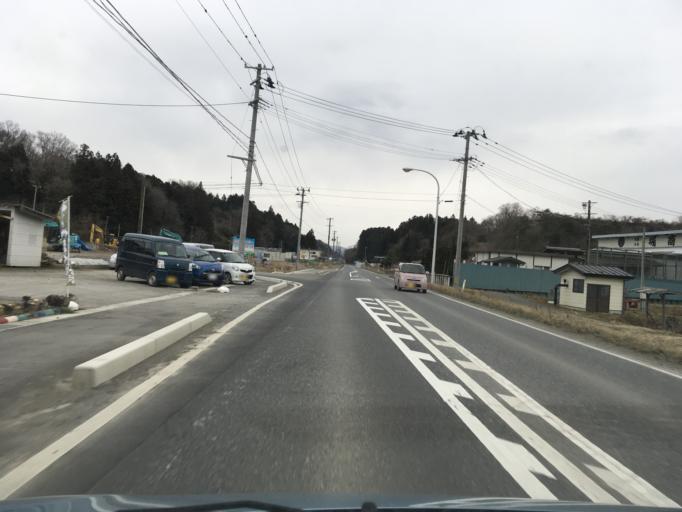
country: JP
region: Miyagi
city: Wakuya
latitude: 38.6709
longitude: 141.2715
